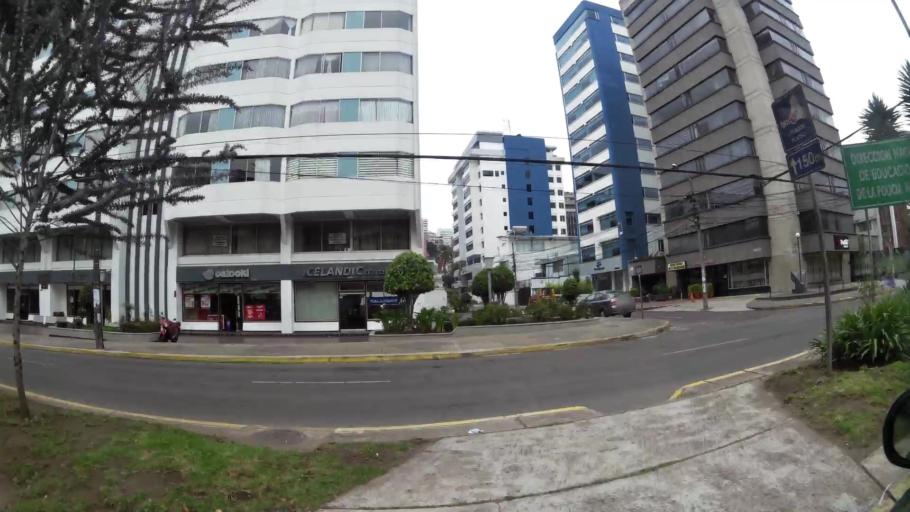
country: EC
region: Pichincha
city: Quito
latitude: -0.1949
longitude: -78.4837
